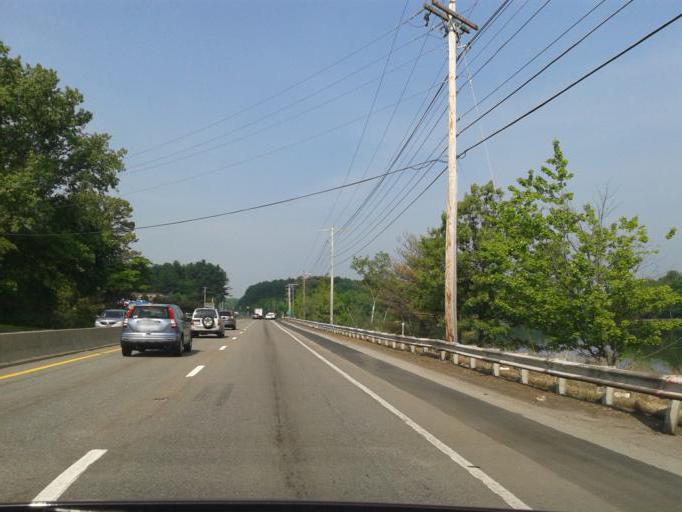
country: US
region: Massachusetts
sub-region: Worcester County
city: Southborough
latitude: 42.2928
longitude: -71.5163
